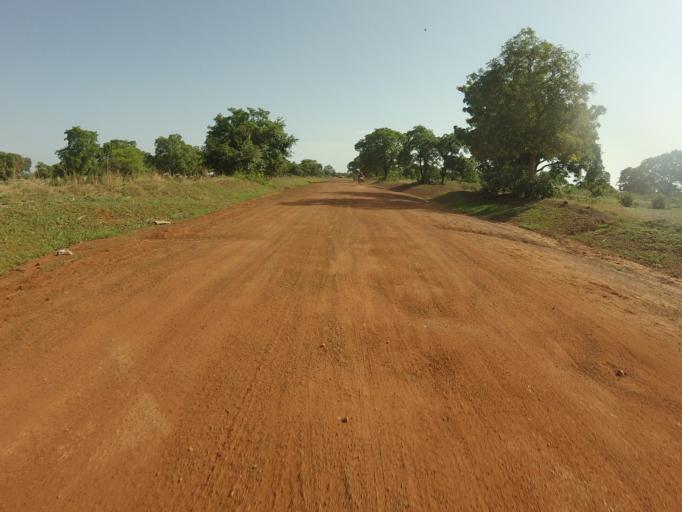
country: GH
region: Upper East
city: Bawku
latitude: 10.7834
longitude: -0.1879
